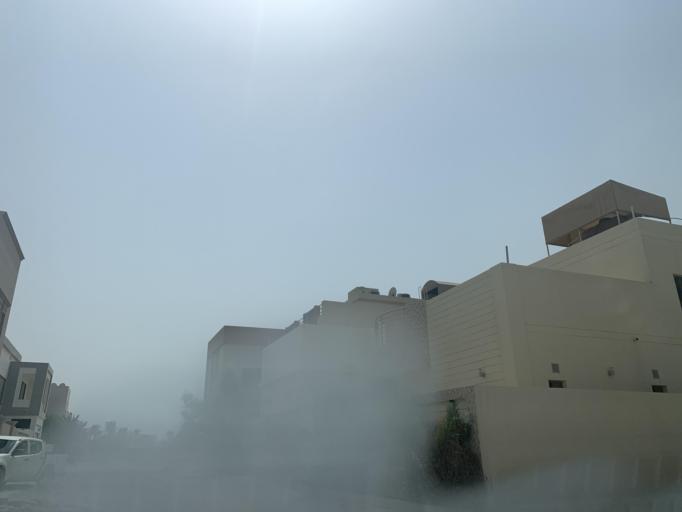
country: BH
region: Manama
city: Jidd Hafs
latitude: 26.2000
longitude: 50.4681
